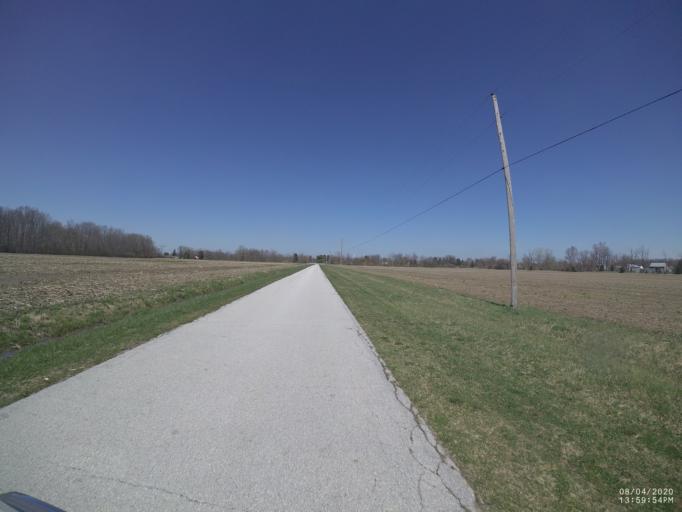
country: US
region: Ohio
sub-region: Sandusky County
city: Gibsonburg
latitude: 41.3078
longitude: -83.2835
